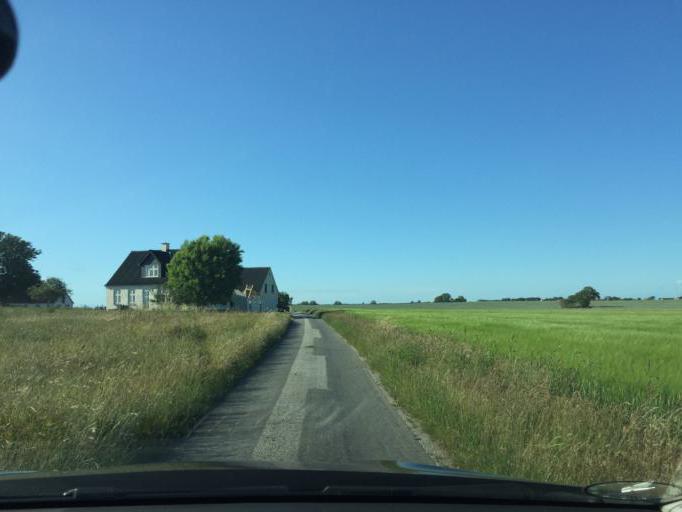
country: DK
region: Zealand
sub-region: Slagelse Kommune
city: Skaelskor
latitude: 55.1977
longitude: 11.1825
